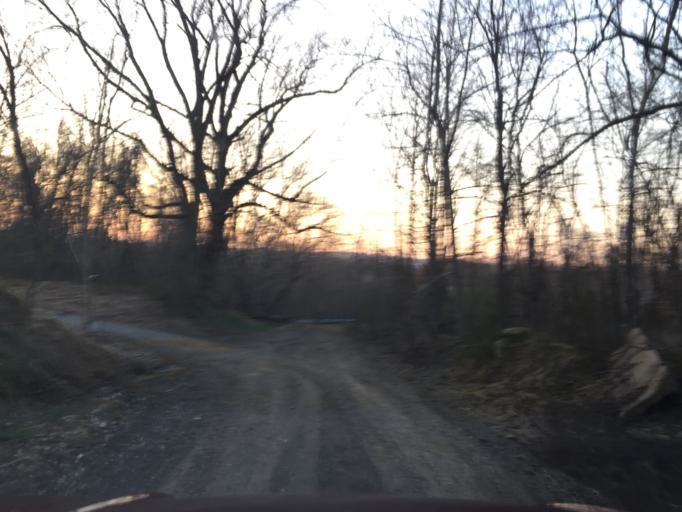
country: US
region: Maryland
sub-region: Frederick County
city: Brunswick
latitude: 39.2930
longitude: -77.6003
